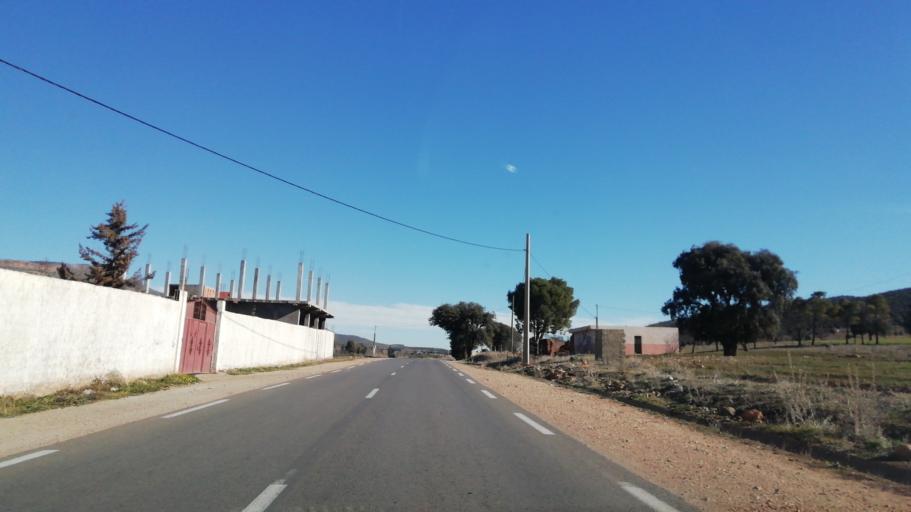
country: DZ
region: Tlemcen
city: Sebdou
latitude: 34.6847
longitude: -1.2508
